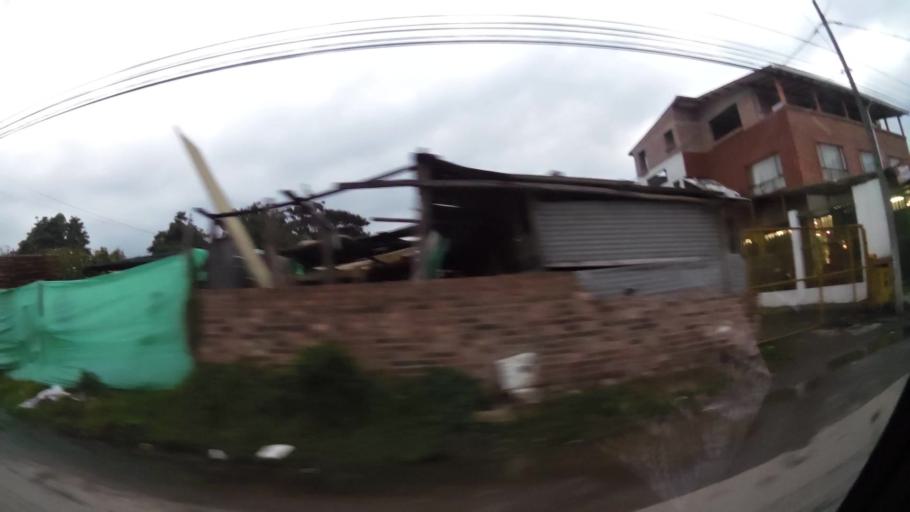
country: CO
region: Cundinamarca
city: Chia
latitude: 4.8423
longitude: -74.0696
